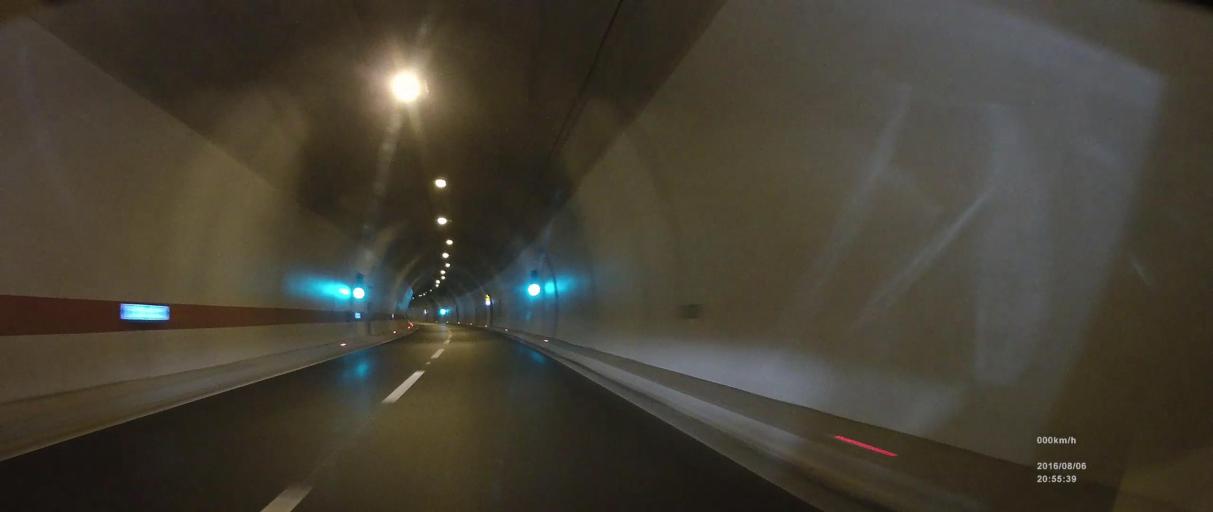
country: BA
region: Federation of Bosnia and Herzegovina
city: Vitina
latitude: 43.1626
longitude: 17.4676
